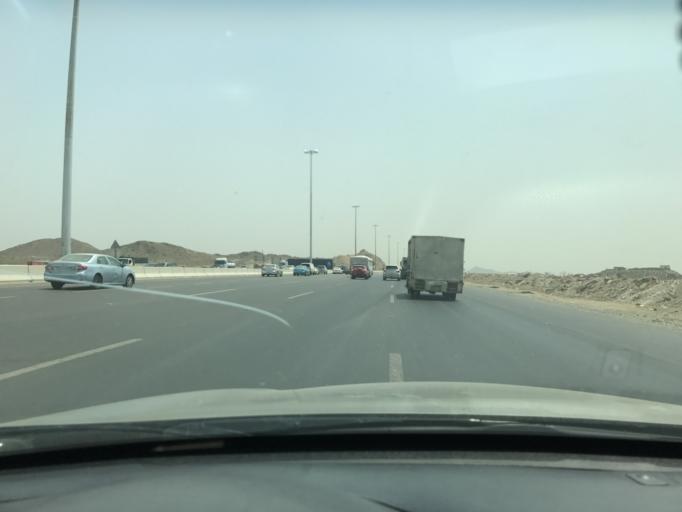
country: SA
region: Makkah
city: Jeddah
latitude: 21.6154
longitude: 39.2524
